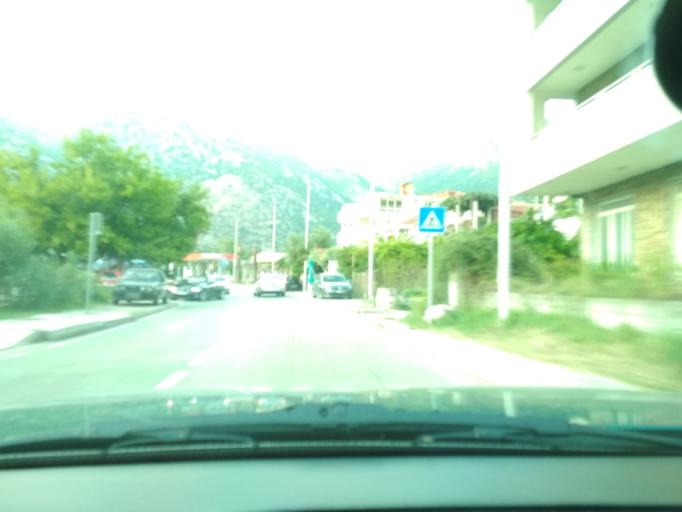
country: ME
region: Kotor
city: Risan
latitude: 42.5098
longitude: 18.6966
